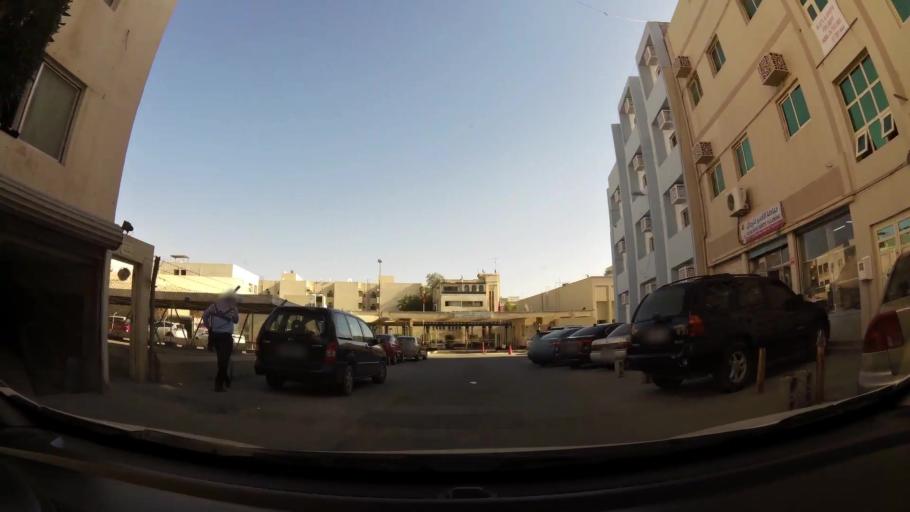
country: BH
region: Manama
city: Manama
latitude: 26.2360
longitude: 50.5835
